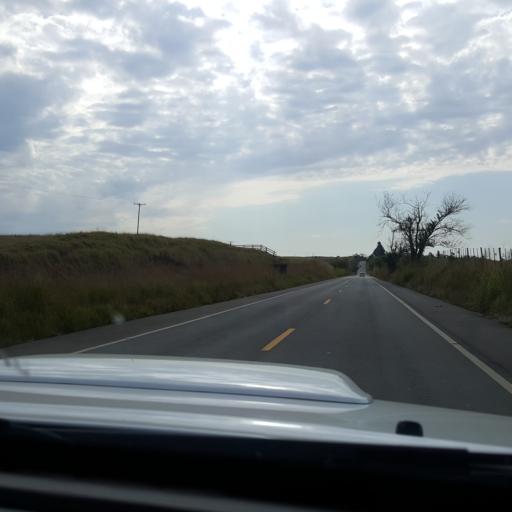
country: BR
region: Sao Paulo
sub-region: Itaporanga
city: Itaporanga
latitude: -23.7588
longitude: -49.4497
